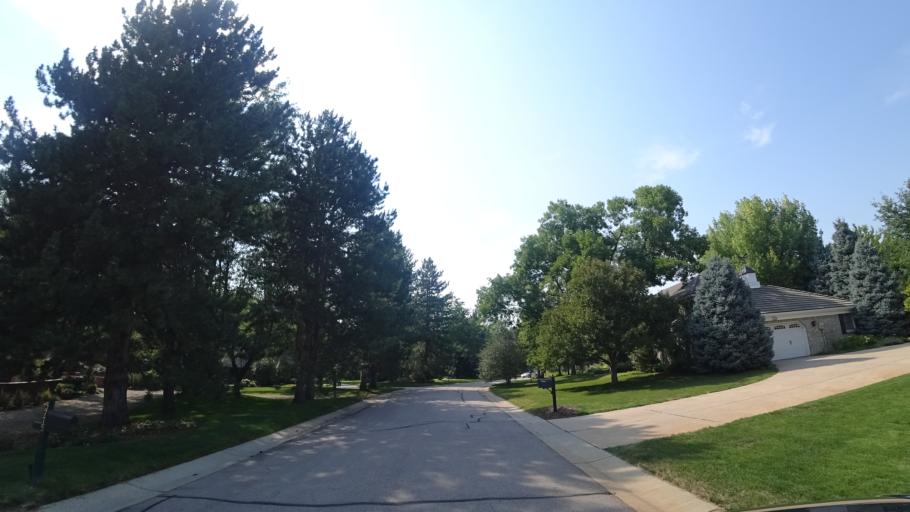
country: US
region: Colorado
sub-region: Arapahoe County
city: Greenwood Village
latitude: 39.6119
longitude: -104.9681
